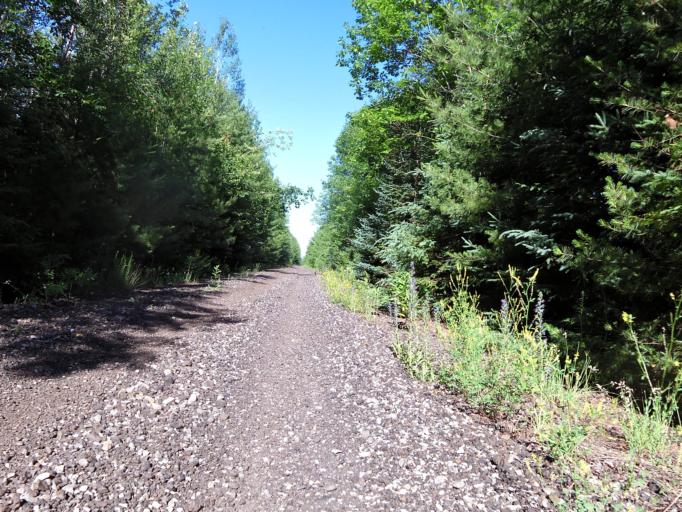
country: CA
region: Ontario
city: Arnprior
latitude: 45.4589
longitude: -76.2468
